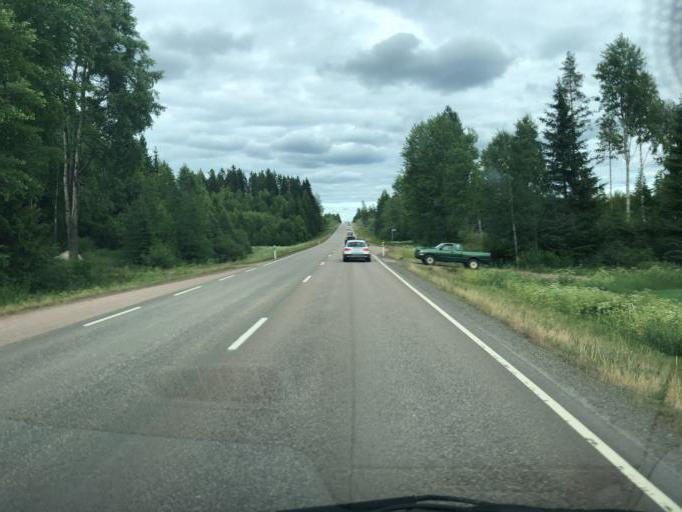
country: FI
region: Kymenlaakso
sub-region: Kouvola
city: Kouvola
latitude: 61.0472
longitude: 27.0218
